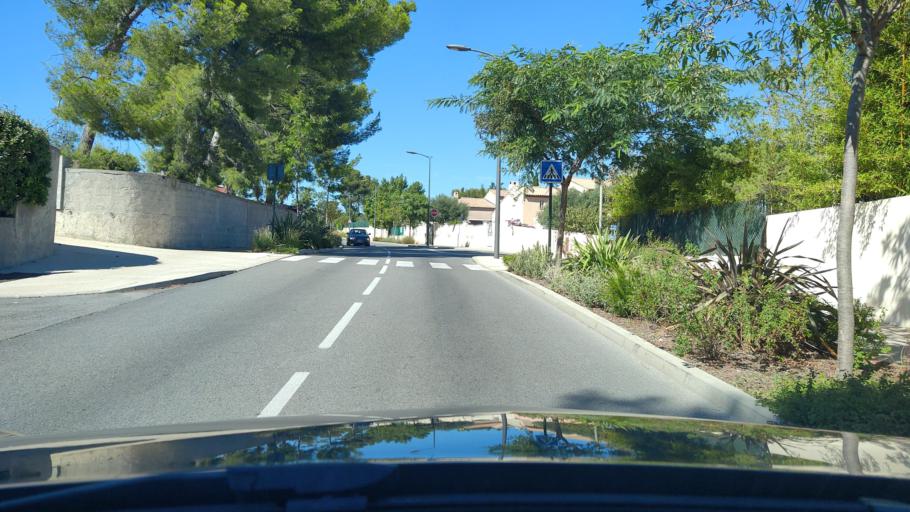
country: FR
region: Provence-Alpes-Cote d'Azur
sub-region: Departement du Var
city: Sanary-sur-Mer
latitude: 43.1312
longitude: 5.7932
